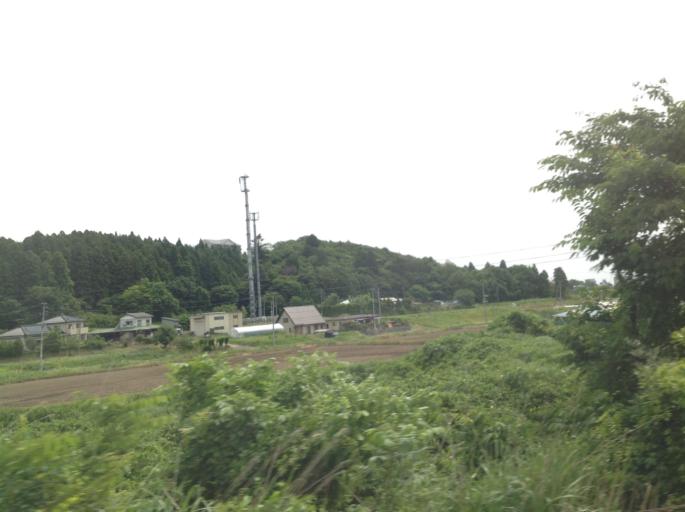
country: JP
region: Miyagi
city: Sendai-shi
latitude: 38.3334
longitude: 140.8560
